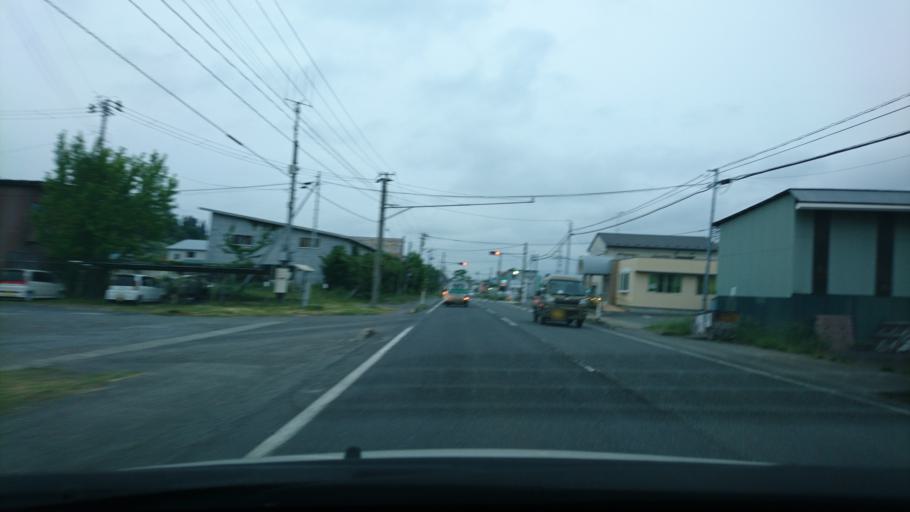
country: JP
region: Iwate
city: Ichinoseki
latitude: 38.9096
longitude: 141.1310
